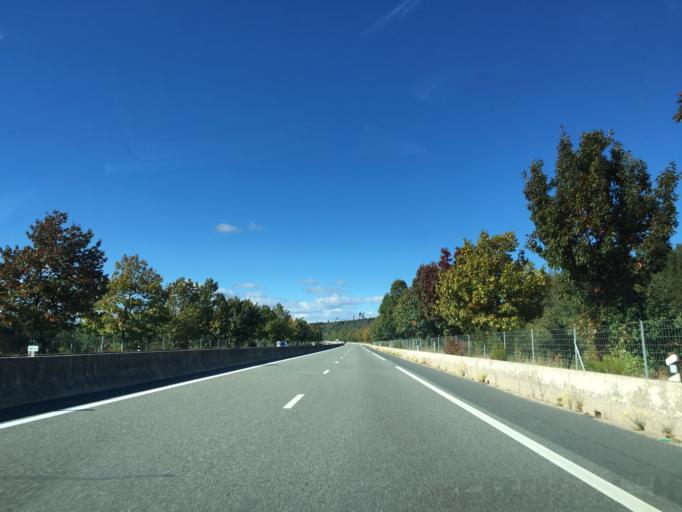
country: FR
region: Lorraine
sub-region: Departement de Meurthe-et-Moselle
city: Baccarat
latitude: 48.4277
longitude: 6.7889
